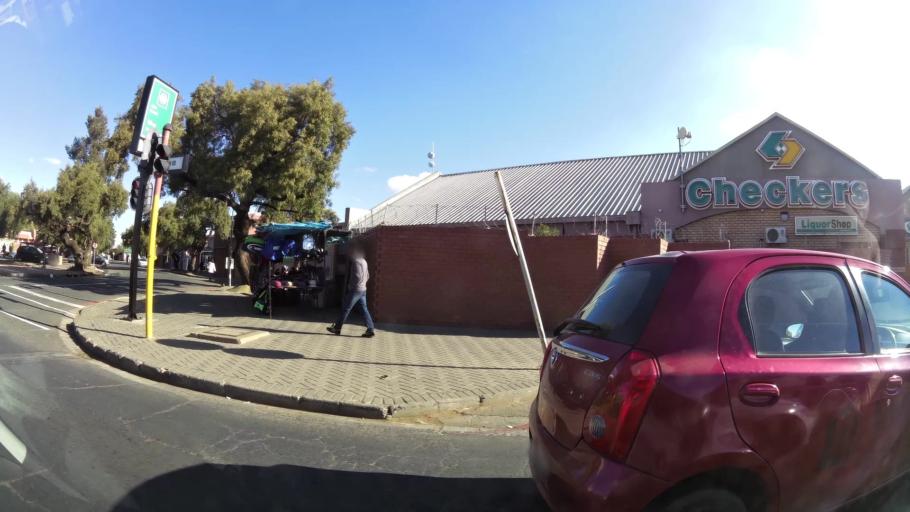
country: ZA
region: Northern Cape
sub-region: Frances Baard District Municipality
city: Kimberley
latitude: -28.7447
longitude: 24.7632
